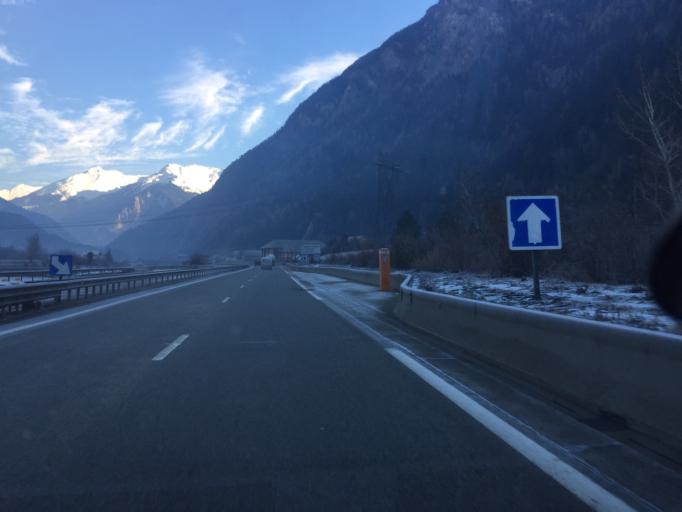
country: FR
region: Rhone-Alpes
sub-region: Departement de la Savoie
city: Modane
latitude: 45.2046
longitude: 6.5811
